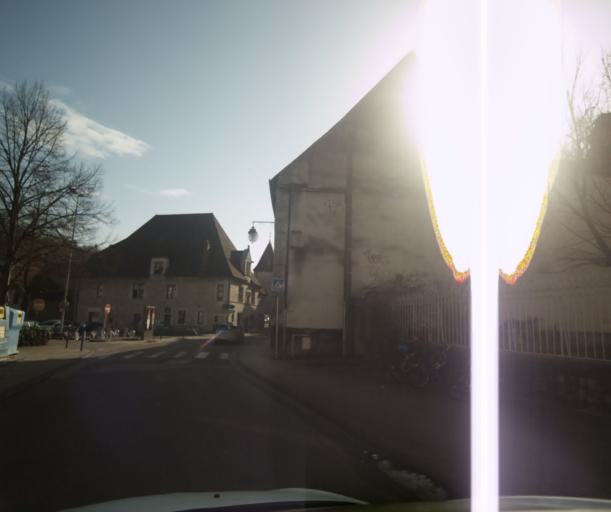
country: FR
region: Franche-Comte
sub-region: Departement du Doubs
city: Besancon
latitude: 47.2347
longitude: 6.0328
